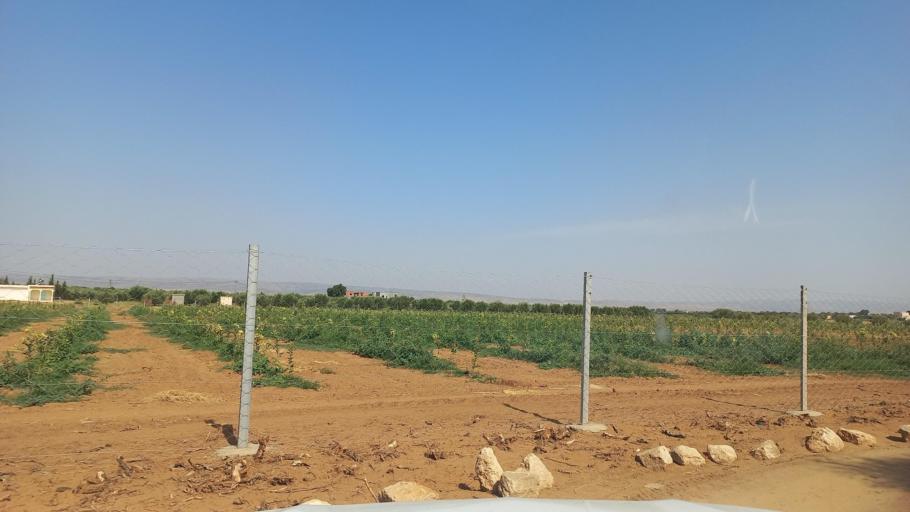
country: TN
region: Al Qasrayn
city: Kasserine
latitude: 35.2393
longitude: 9.0501
